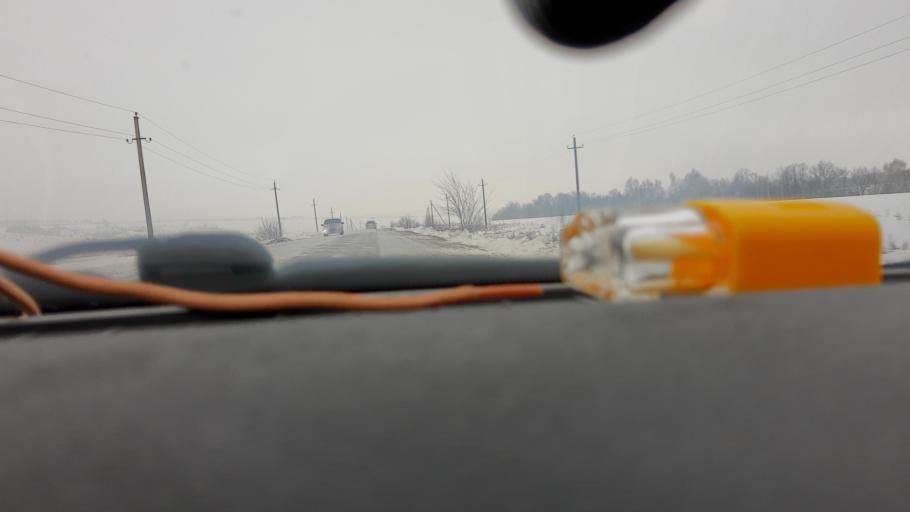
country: RU
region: Bashkortostan
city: Ulukulevo
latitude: 54.5385
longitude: 56.4316
